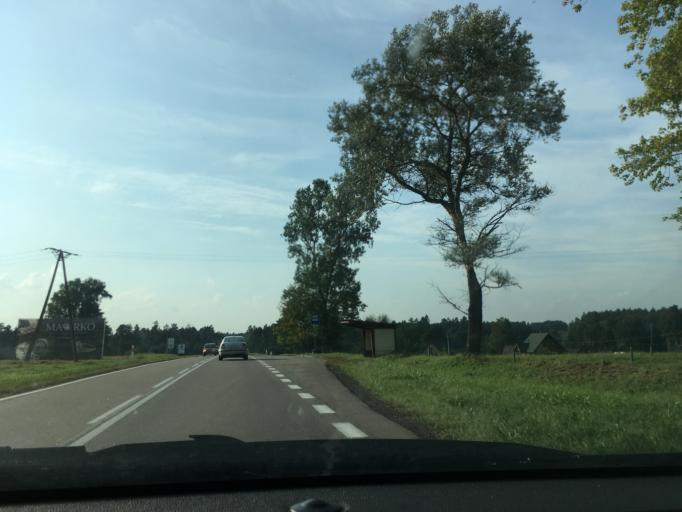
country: PL
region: Podlasie
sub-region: Powiat bialostocki
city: Dobrzyniewo Duze
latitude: 53.2565
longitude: 22.9797
